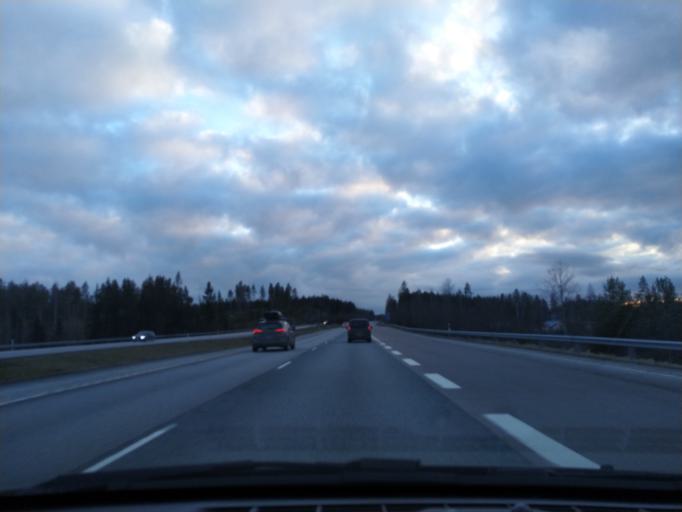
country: FI
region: Uusimaa
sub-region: Helsinki
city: Maentsaelae
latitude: 60.6906
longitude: 25.3932
